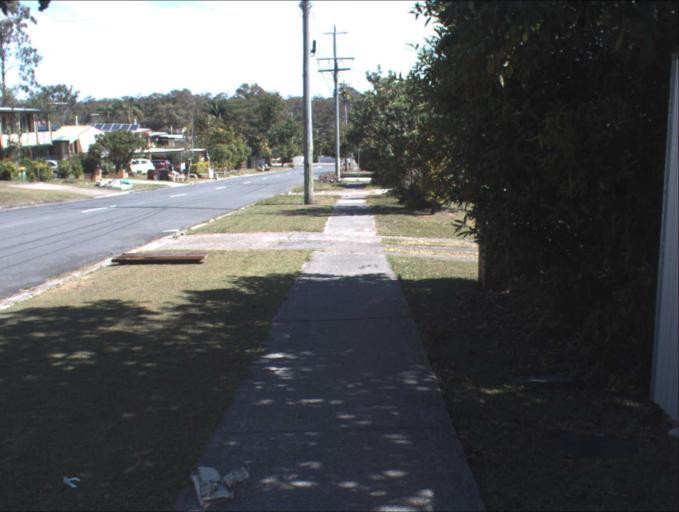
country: AU
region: Queensland
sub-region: Logan
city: Slacks Creek
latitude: -27.6498
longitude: 153.1285
